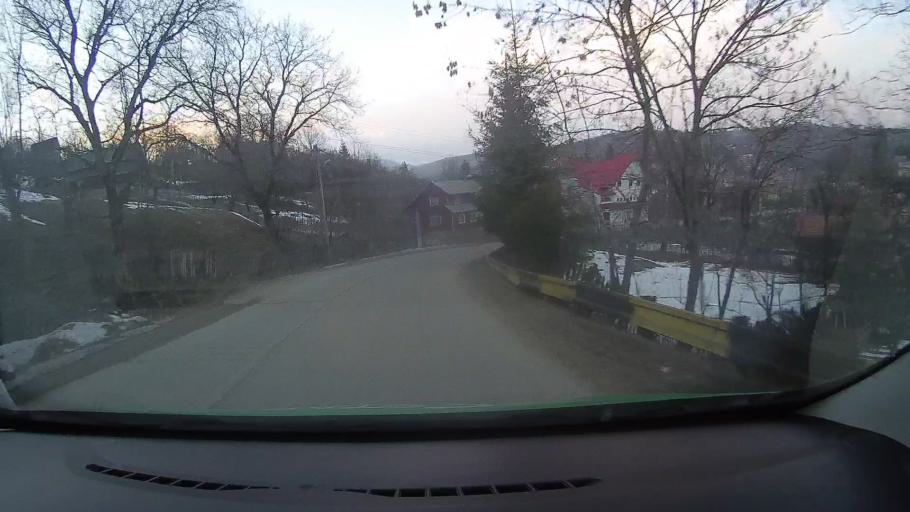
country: RO
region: Prahova
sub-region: Comuna Secaria
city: Secaria
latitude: 45.2715
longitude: 25.6852
